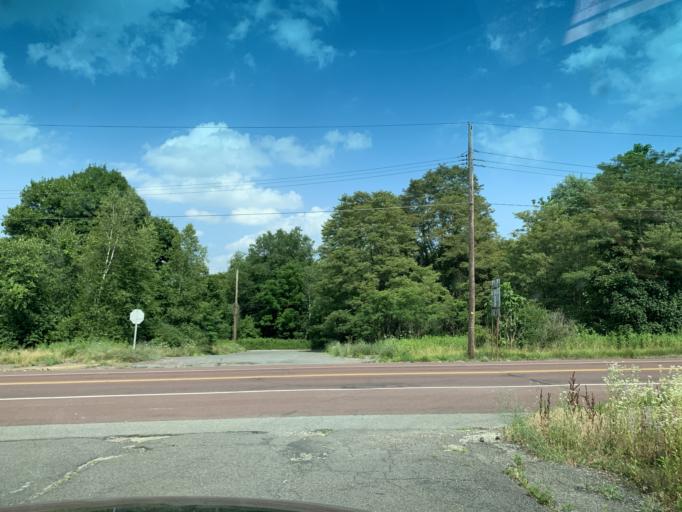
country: US
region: Pennsylvania
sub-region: Schuylkill County
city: Ashland
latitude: 40.8031
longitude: -76.3410
